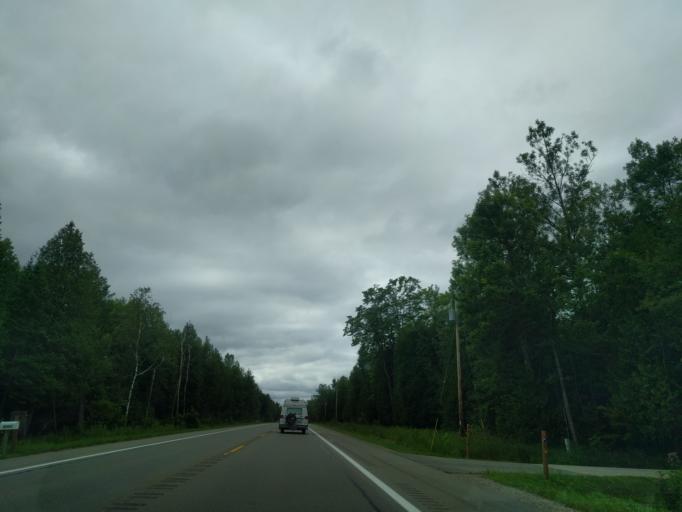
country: US
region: Michigan
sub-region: Menominee County
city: Menominee
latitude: 45.3141
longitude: -87.4351
